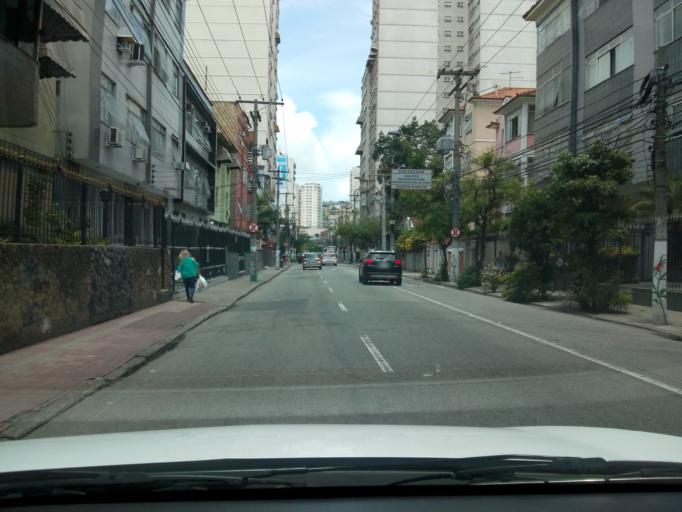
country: BR
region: Rio de Janeiro
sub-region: Niteroi
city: Niteroi
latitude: -22.9062
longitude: -43.1076
